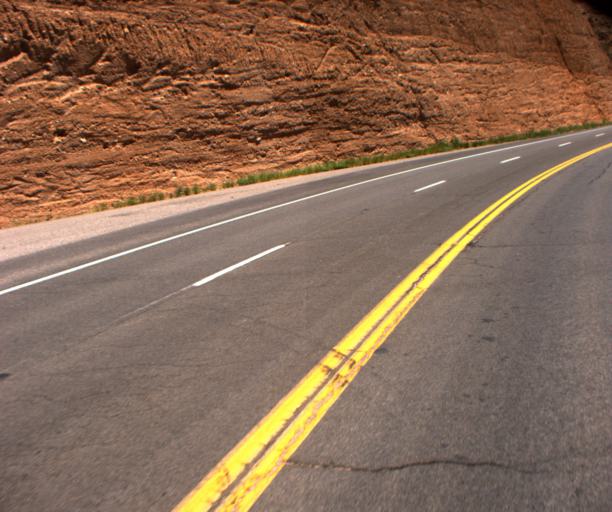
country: US
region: Arizona
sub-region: Greenlee County
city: Clifton
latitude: 33.0669
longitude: -109.3274
